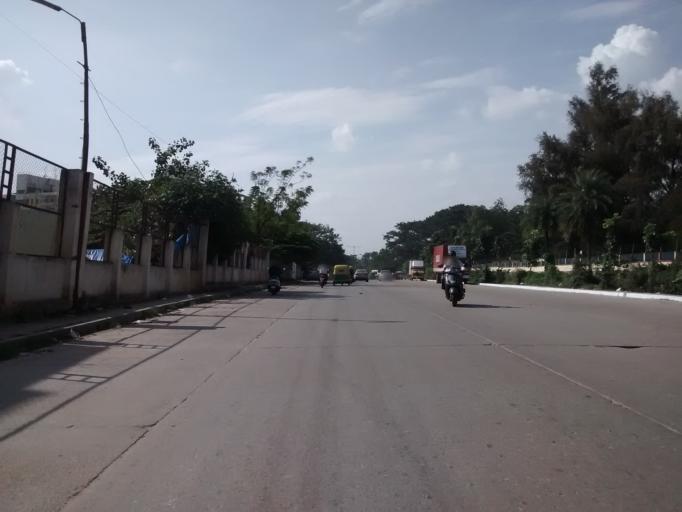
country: IN
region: Karnataka
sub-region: Bangalore Urban
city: Bangalore
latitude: 12.9821
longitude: 77.6502
